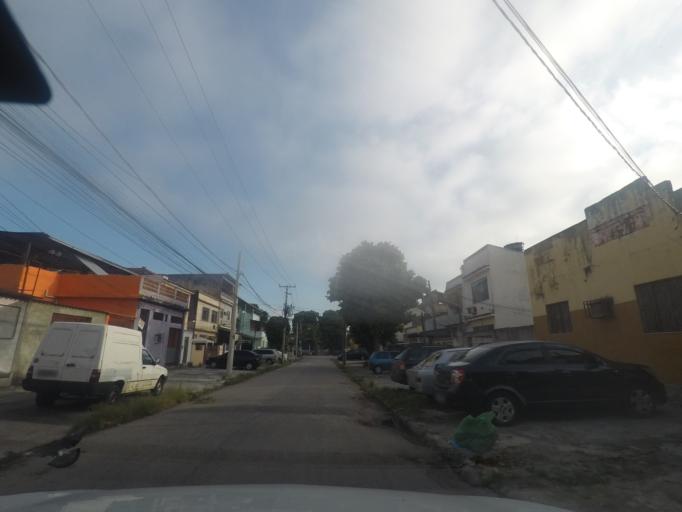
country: BR
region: Rio de Janeiro
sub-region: Duque De Caxias
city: Duque de Caxias
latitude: -22.8367
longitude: -43.2713
